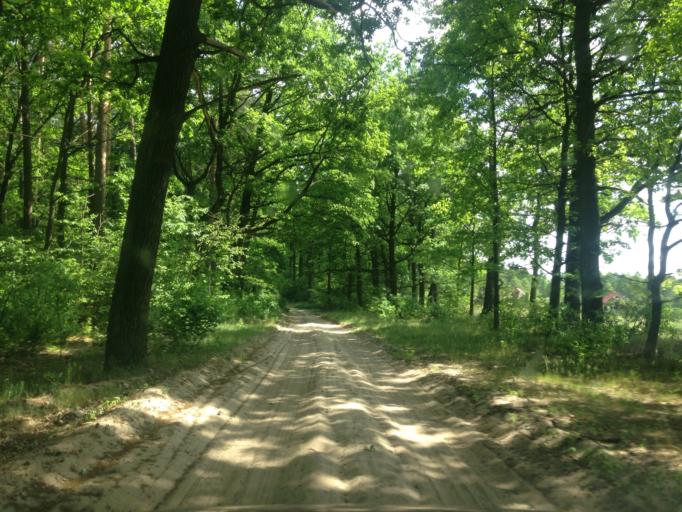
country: PL
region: Kujawsko-Pomorskie
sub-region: Powiat brodnicki
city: Gorzno
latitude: 53.1781
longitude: 19.6499
